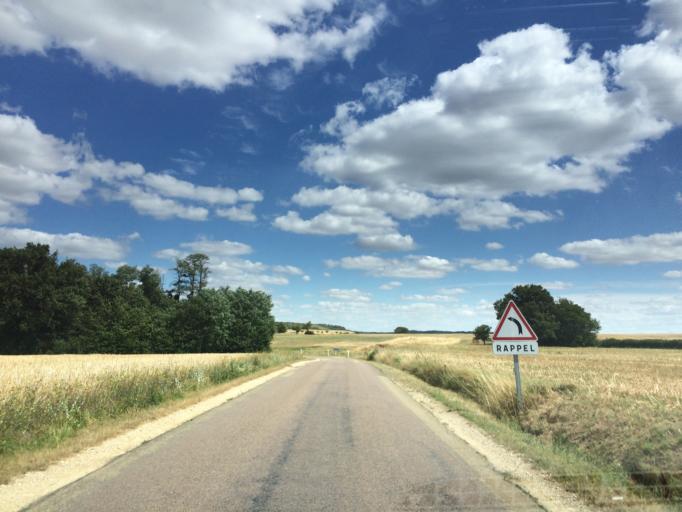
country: FR
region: Bourgogne
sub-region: Departement de l'Yonne
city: Fleury-la-Vallee
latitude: 47.8669
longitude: 3.4184
